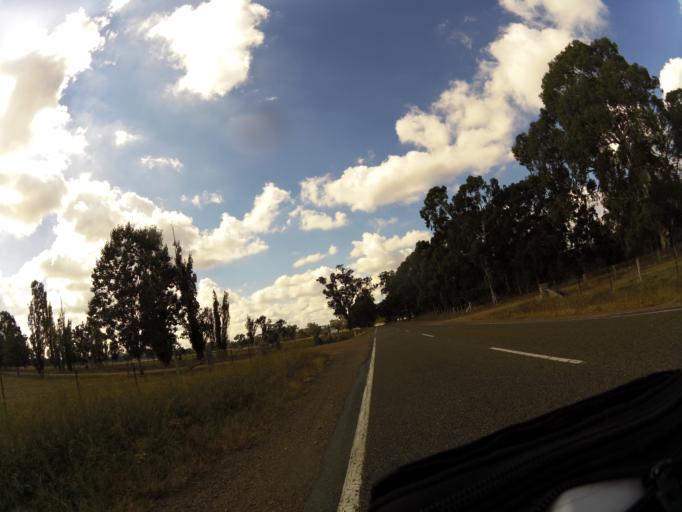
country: AU
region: Victoria
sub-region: Benalla
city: Benalla
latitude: -36.6136
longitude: 146.0246
